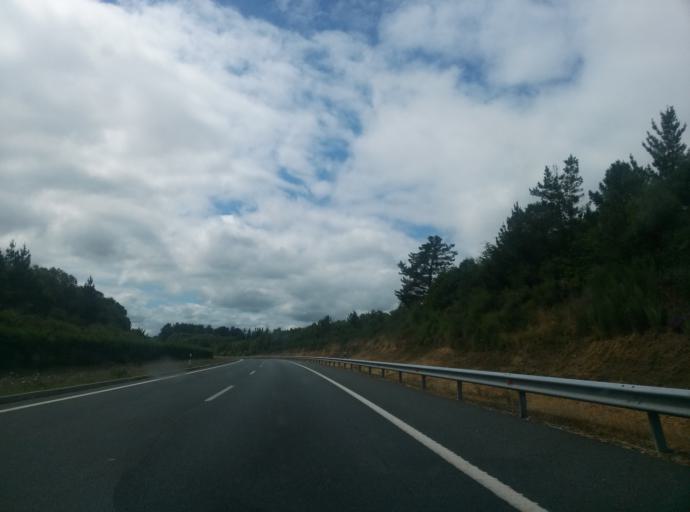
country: ES
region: Galicia
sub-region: Provincia de Lugo
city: Begonte
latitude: 43.1508
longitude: -7.6608
